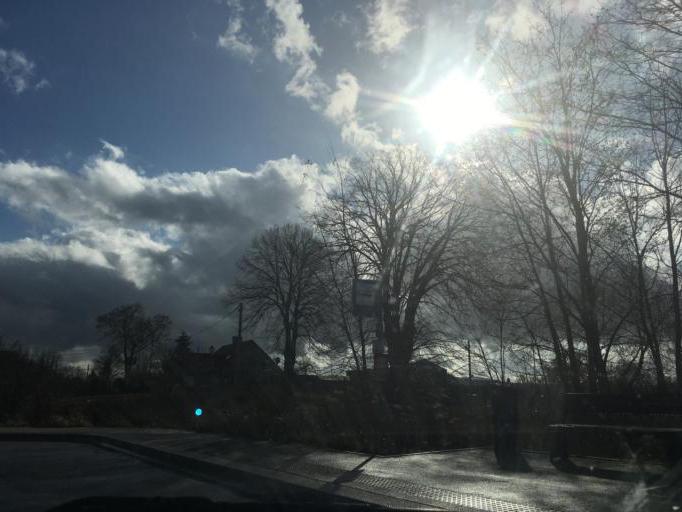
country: PL
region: Pomeranian Voivodeship
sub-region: Powiat gdanski
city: Cedry Wielkie
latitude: 54.3509
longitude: 18.7908
